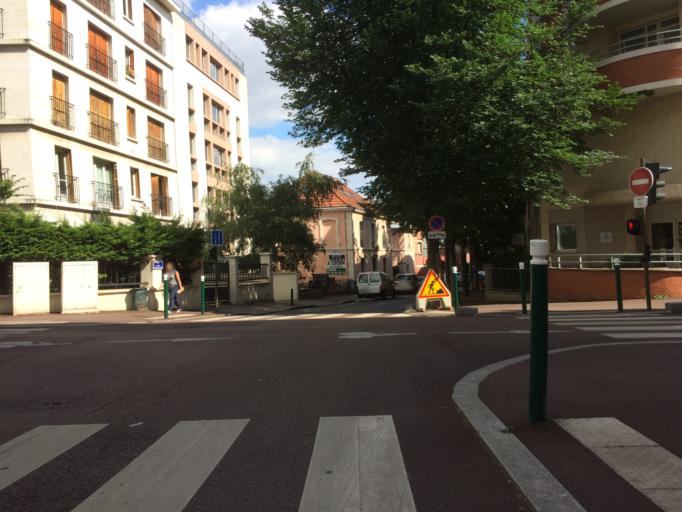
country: FR
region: Ile-de-France
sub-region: Departement des Hauts-de-Seine
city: Suresnes
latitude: 48.8731
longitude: 2.2261
